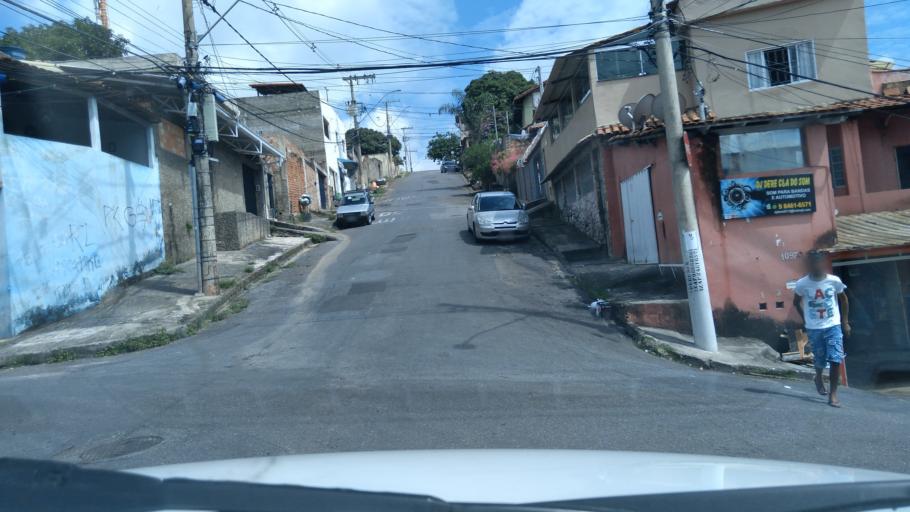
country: BR
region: Minas Gerais
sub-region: Belo Horizonte
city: Belo Horizonte
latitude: -19.9002
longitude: -43.8892
